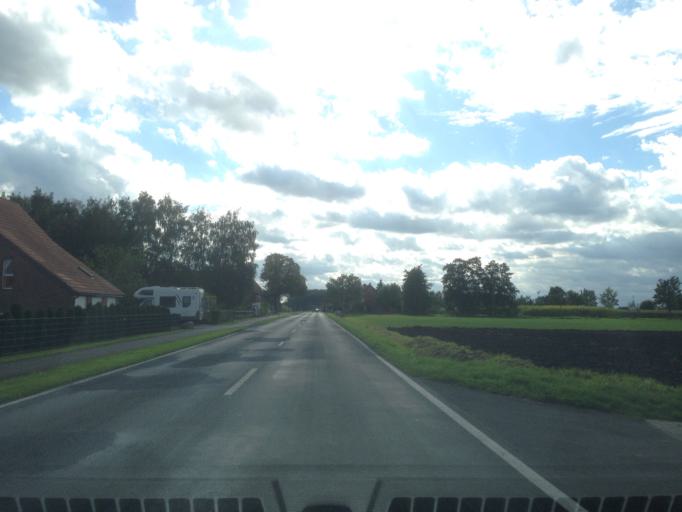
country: DE
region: North Rhine-Westphalia
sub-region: Regierungsbezirk Munster
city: Senden
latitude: 51.8158
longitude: 7.5003
